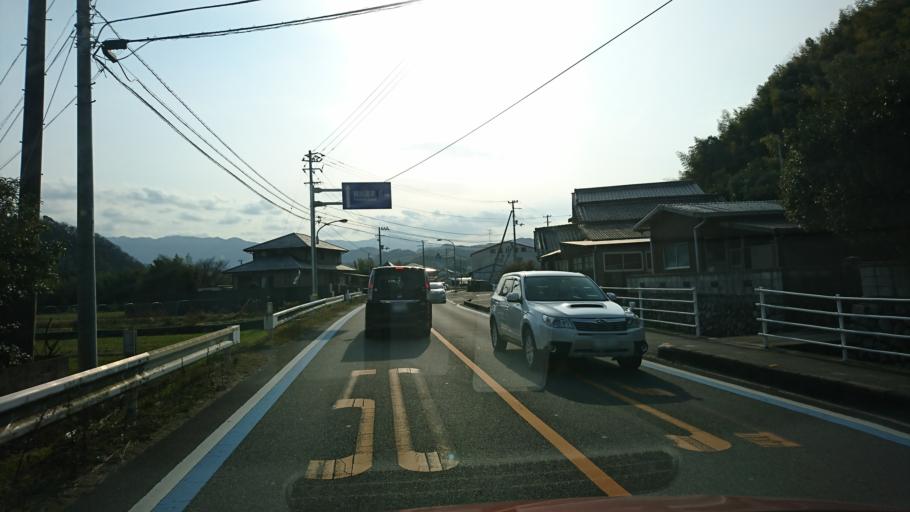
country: JP
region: Ehime
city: Hojo
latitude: 34.0246
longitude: 132.9462
